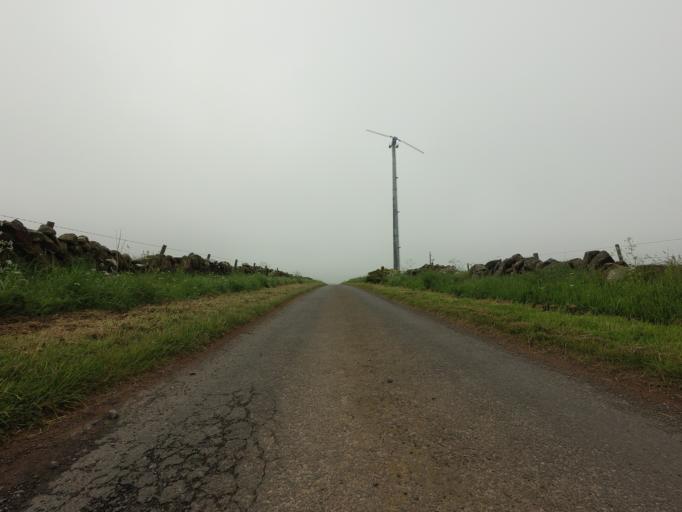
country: GB
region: Scotland
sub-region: Perth and Kinross
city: Abernethy
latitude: 56.2561
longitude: -3.3227
